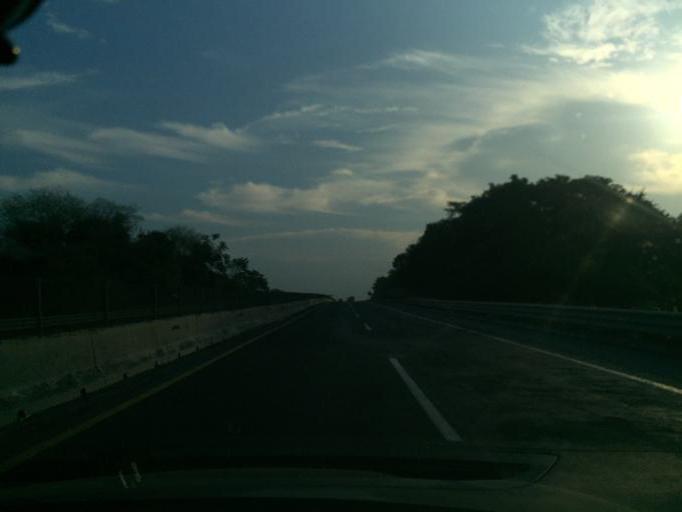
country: MX
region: Veracruz
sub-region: Tierra Blanca
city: Huixcolotla
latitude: 18.7853
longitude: -96.5032
